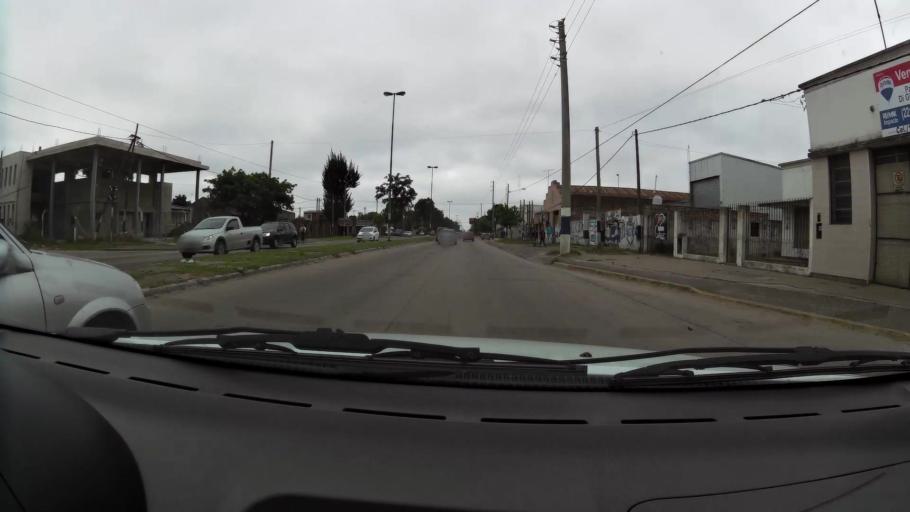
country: AR
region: Buenos Aires
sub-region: Partido de La Plata
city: La Plata
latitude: -34.9613
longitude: -58.0107
